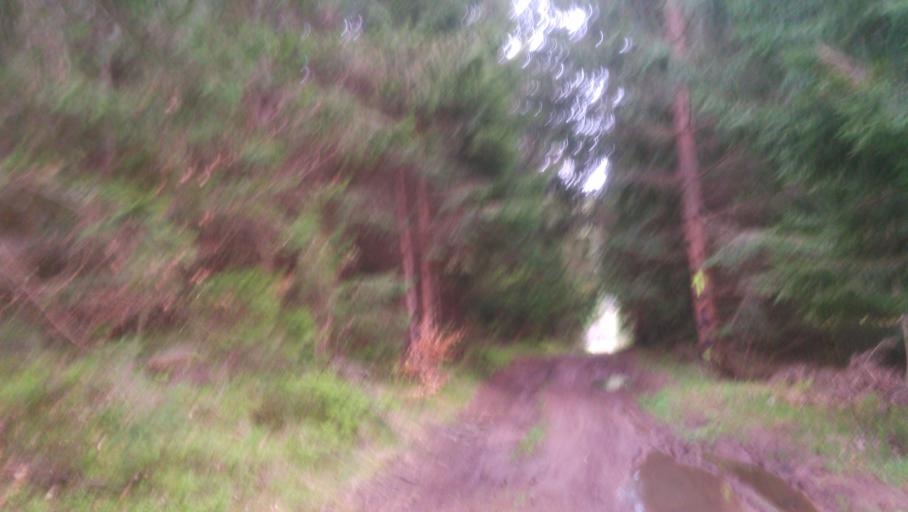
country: SK
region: Banskobystricky
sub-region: Okres Banska Bystrica
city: Brezno
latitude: 48.8748
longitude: 19.5741
